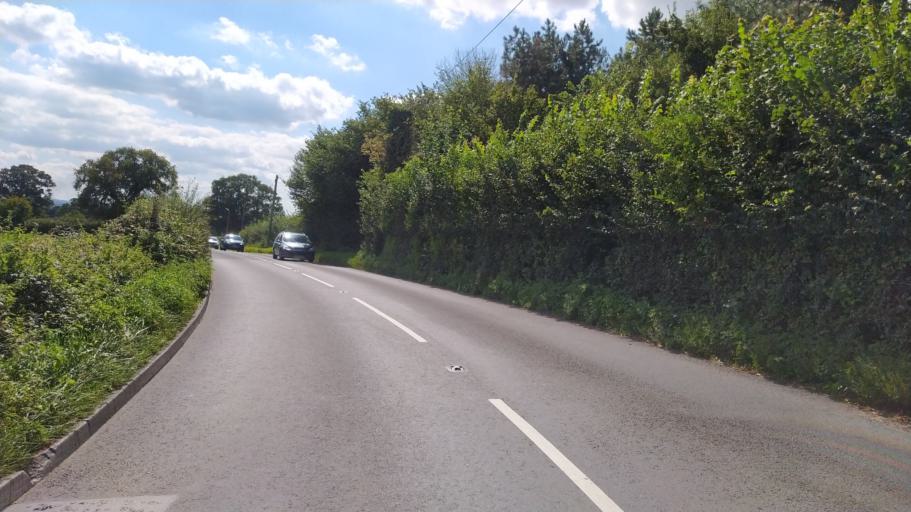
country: GB
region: England
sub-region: Wiltshire
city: Mere
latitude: 51.0876
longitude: -2.2818
